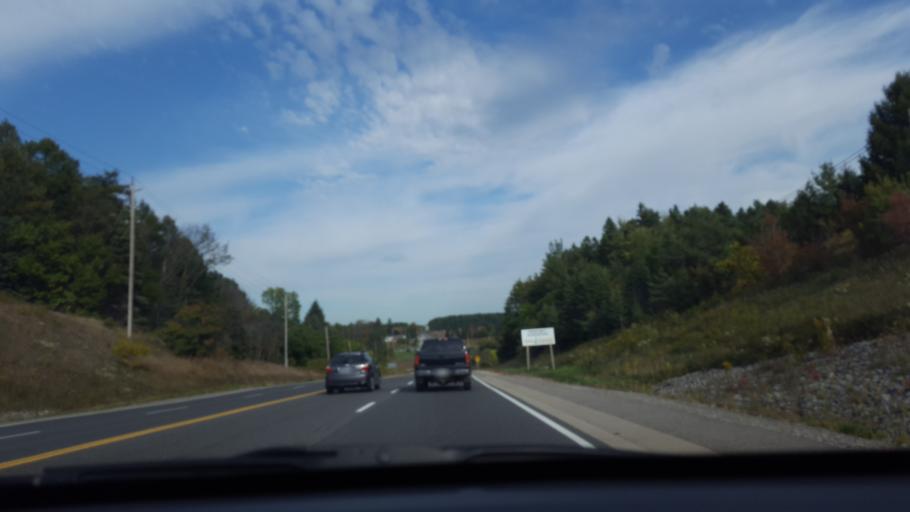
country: CA
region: Ontario
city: Vaughan
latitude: 43.9217
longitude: -79.5603
